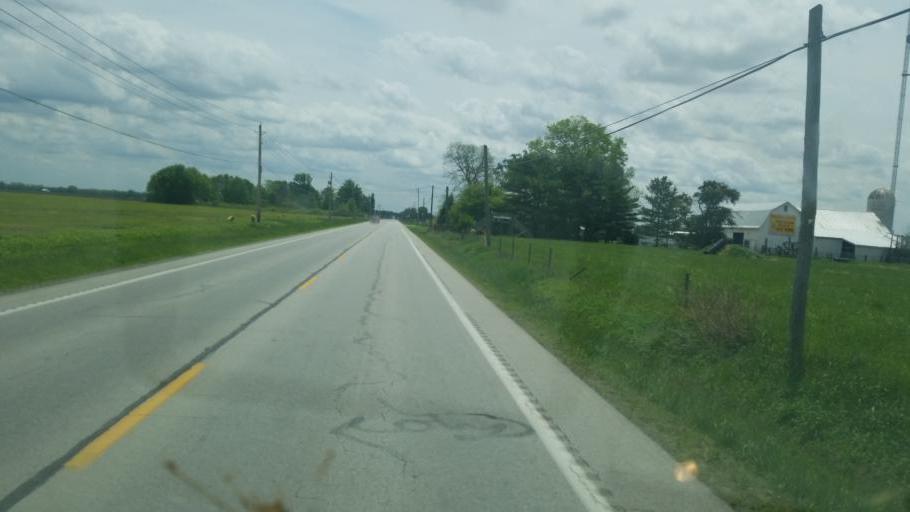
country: US
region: Ohio
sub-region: Sandusky County
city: Ballville
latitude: 41.2304
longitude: -83.1678
